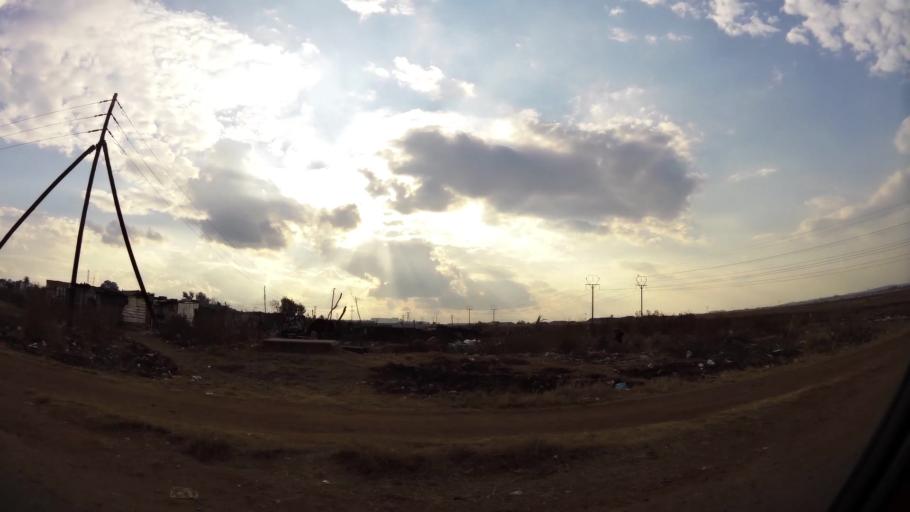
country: ZA
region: Gauteng
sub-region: Sedibeng District Municipality
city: Vanderbijlpark
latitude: -26.6613
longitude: 27.8661
